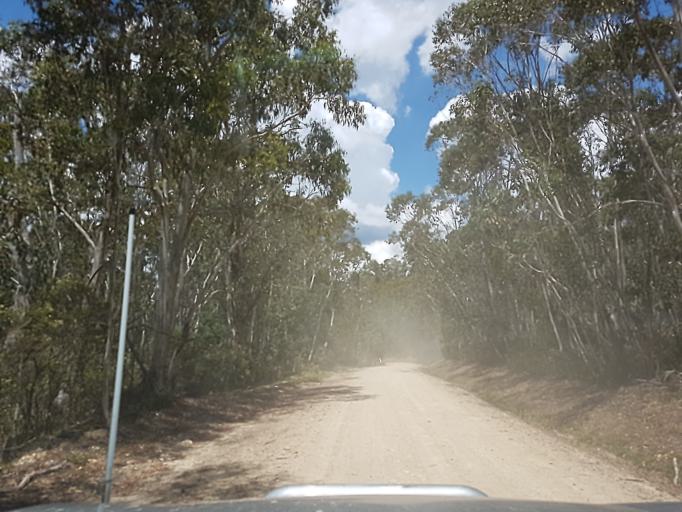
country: AU
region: New South Wales
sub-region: Snowy River
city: Jindabyne
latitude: -36.8797
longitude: 148.0845
